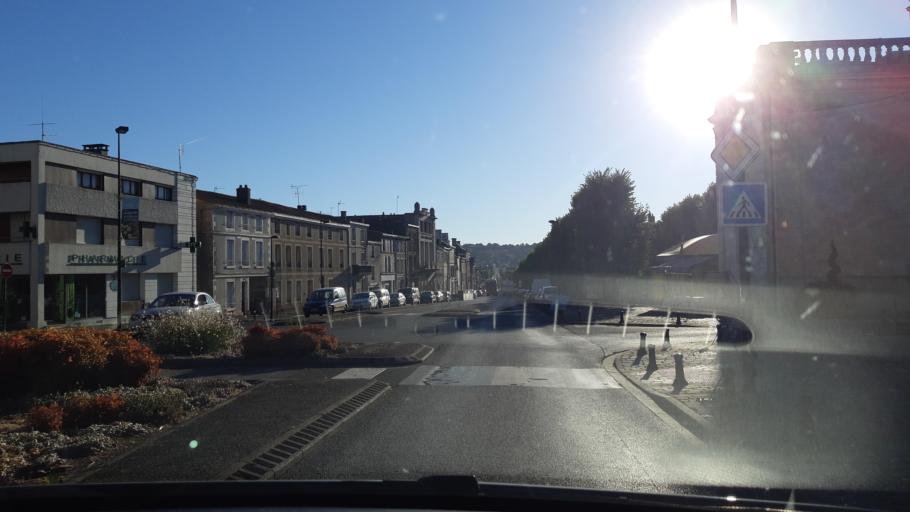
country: FR
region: Poitou-Charentes
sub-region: Departement des Deux-Sevres
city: Exireuil
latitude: 46.4131
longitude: -0.2059
